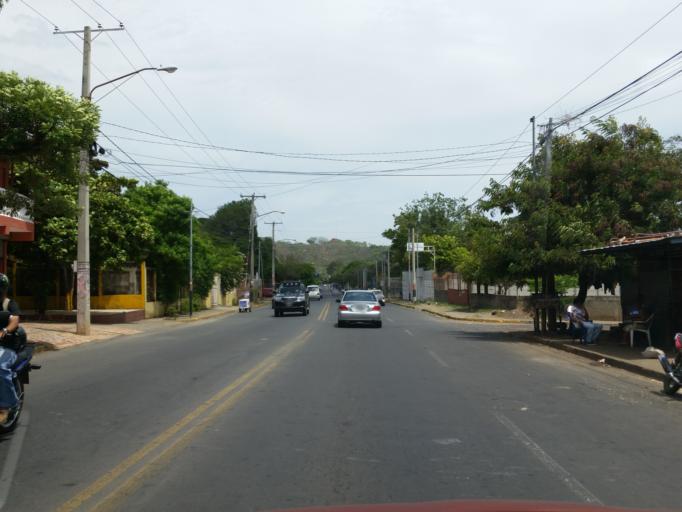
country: NI
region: Managua
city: Managua
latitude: 12.1381
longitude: -86.2624
